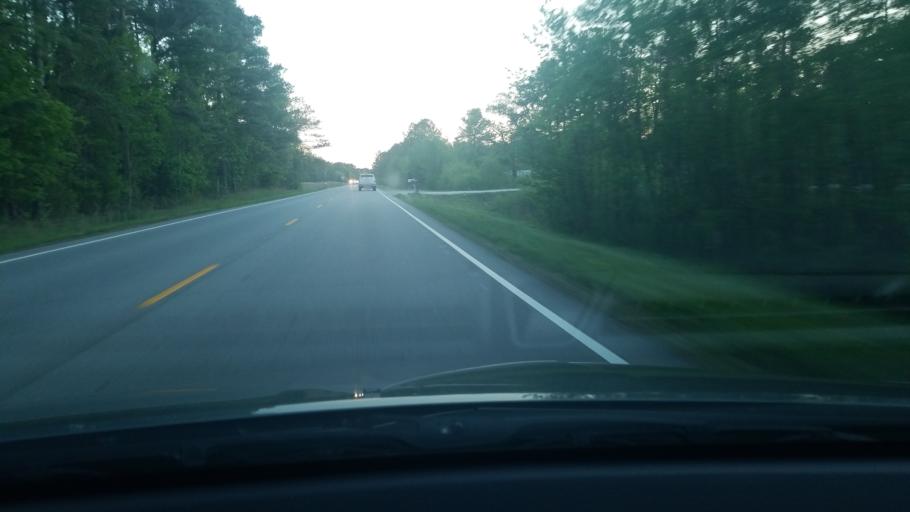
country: US
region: North Carolina
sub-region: Craven County
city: Vanceboro
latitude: 35.2413
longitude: -77.0981
